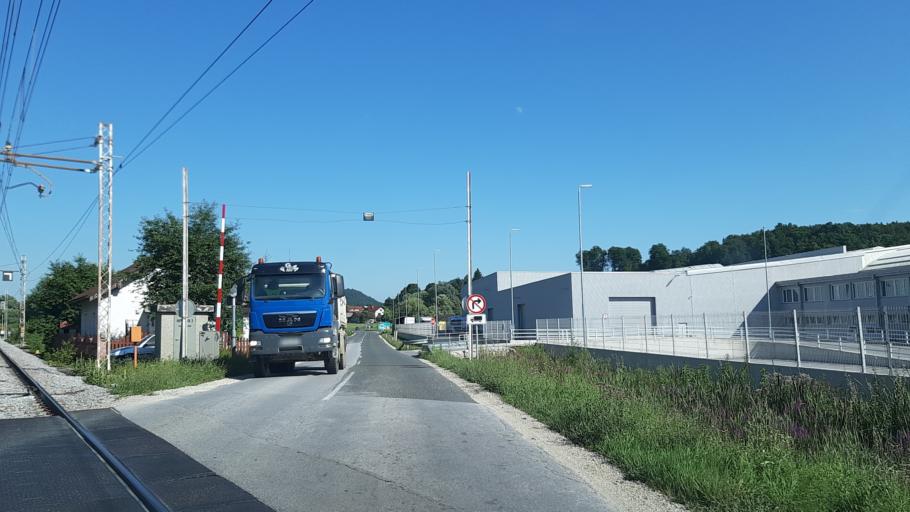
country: SI
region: Sentjur pri Celju
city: Sentjur
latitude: 46.2124
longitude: 15.4047
